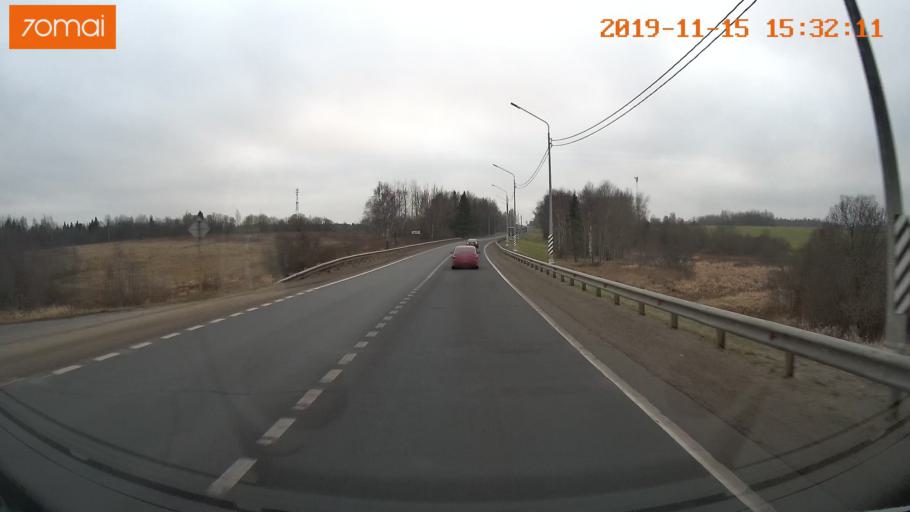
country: RU
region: Jaroslavl
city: Danilov
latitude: 58.0926
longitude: 40.1027
